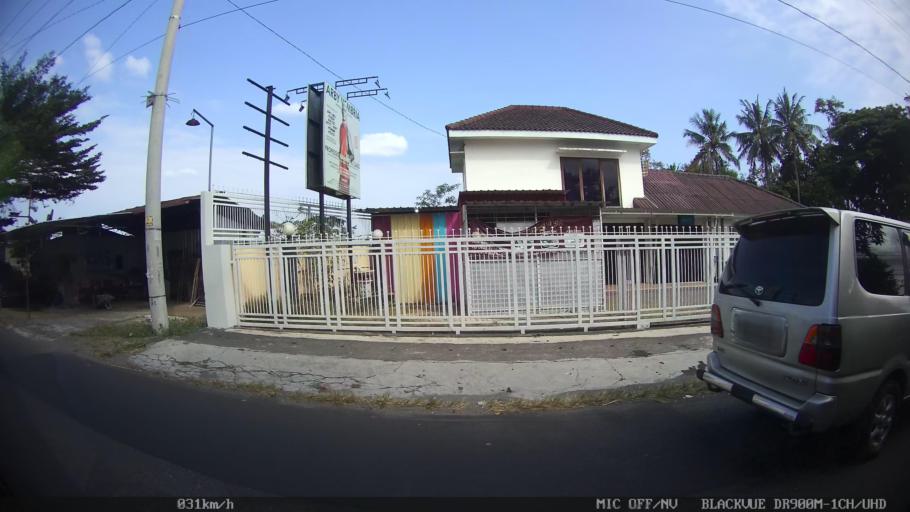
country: ID
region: Daerah Istimewa Yogyakarta
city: Depok
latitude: -7.7300
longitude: 110.4075
